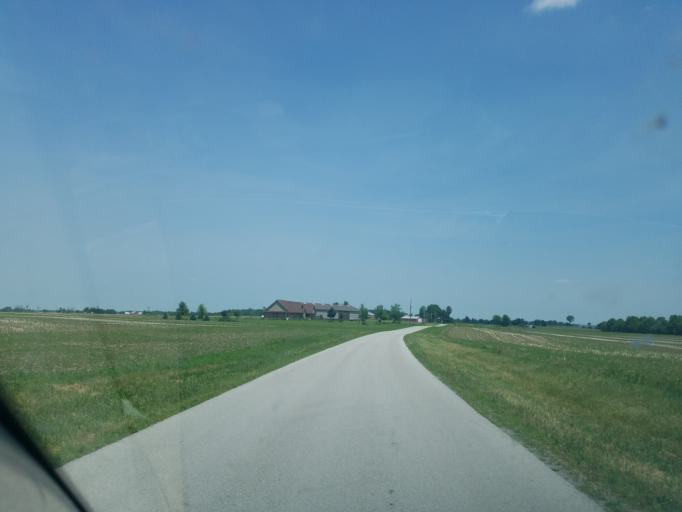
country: US
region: Ohio
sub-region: Wyandot County
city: Carey
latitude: 40.9498
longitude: -83.4951
